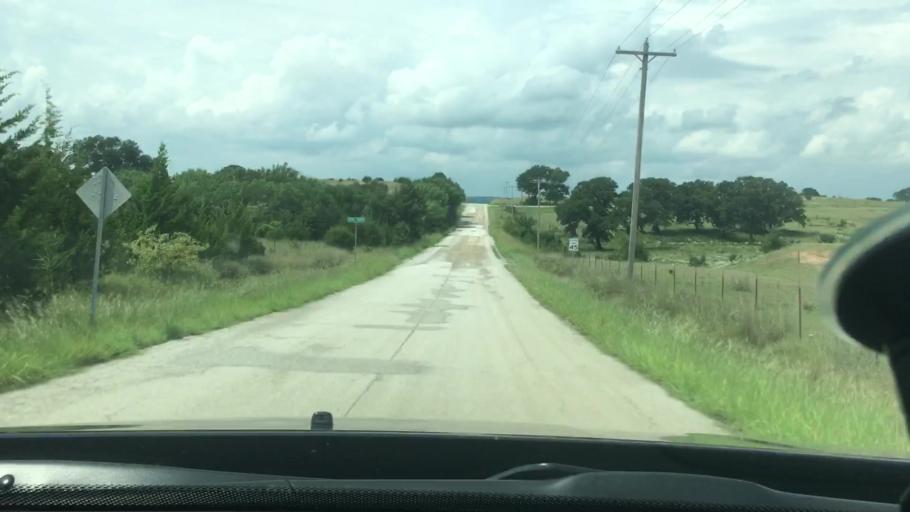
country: US
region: Oklahoma
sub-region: Carter County
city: Dickson
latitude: 34.2527
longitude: -96.9306
